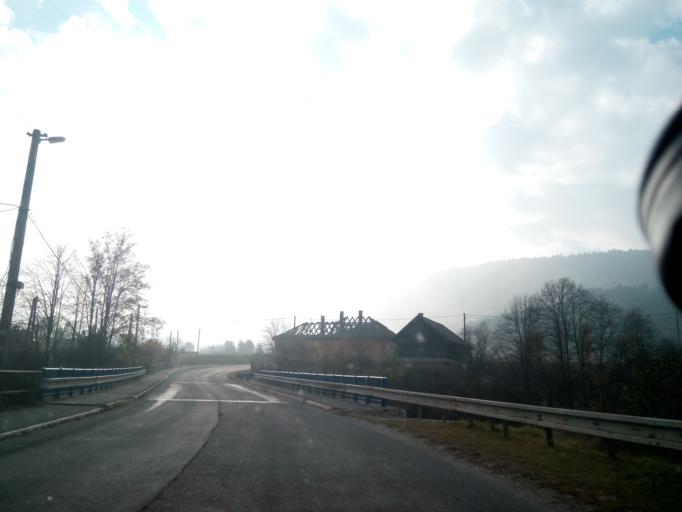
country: SK
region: Kosicky
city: Krompachy
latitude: 48.9230
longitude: 20.9321
